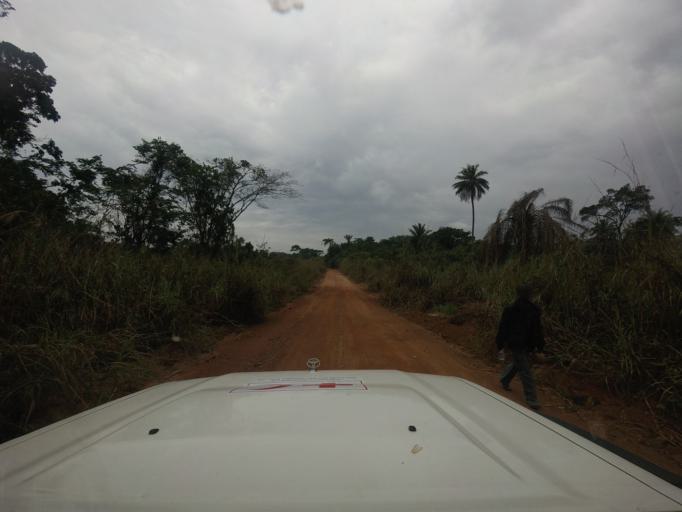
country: SL
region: Eastern Province
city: Buedu
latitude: 8.2803
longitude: -10.1064
